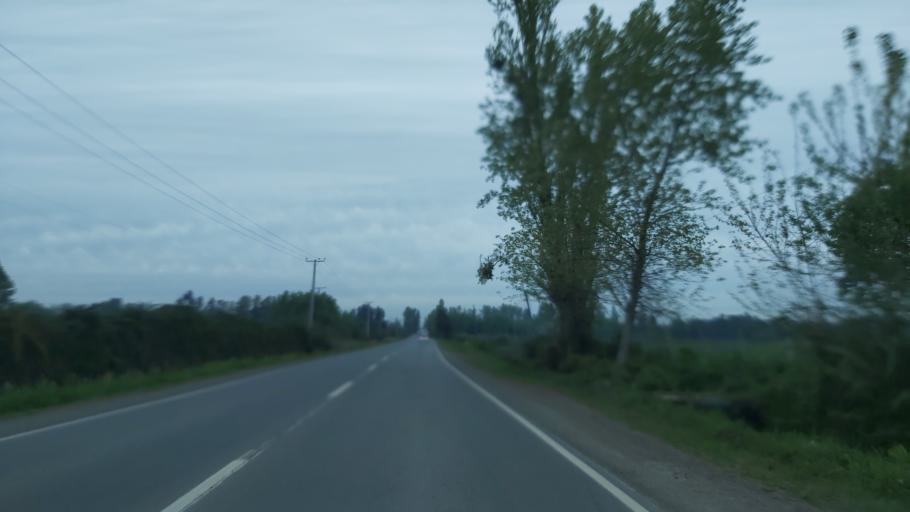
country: CL
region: Maule
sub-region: Provincia de Linares
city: Colbun
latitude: -35.7466
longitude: -71.4930
